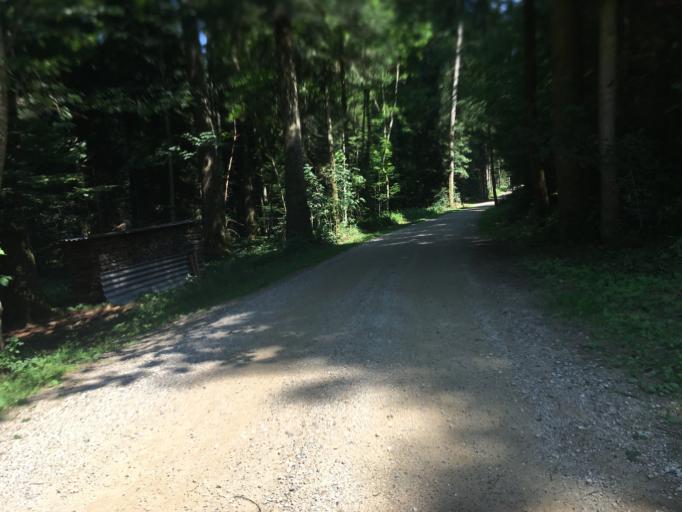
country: CH
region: Bern
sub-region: Emmental District
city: Langnau
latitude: 46.9382
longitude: 7.7601
